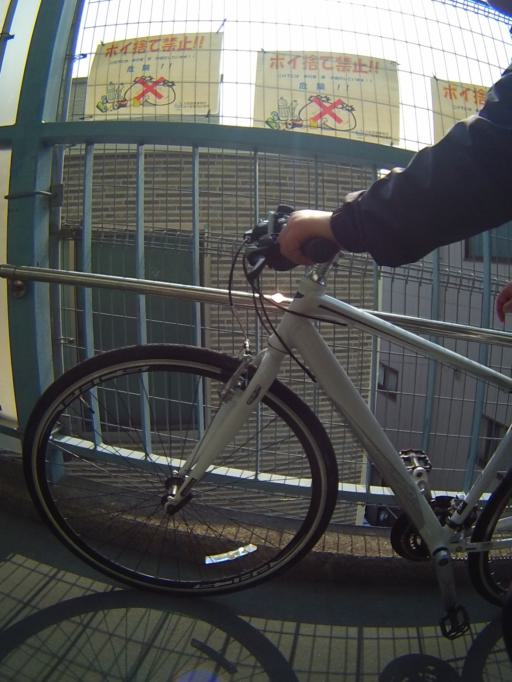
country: JP
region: Osaka
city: Osaka-shi
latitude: 34.6619
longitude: 135.4661
